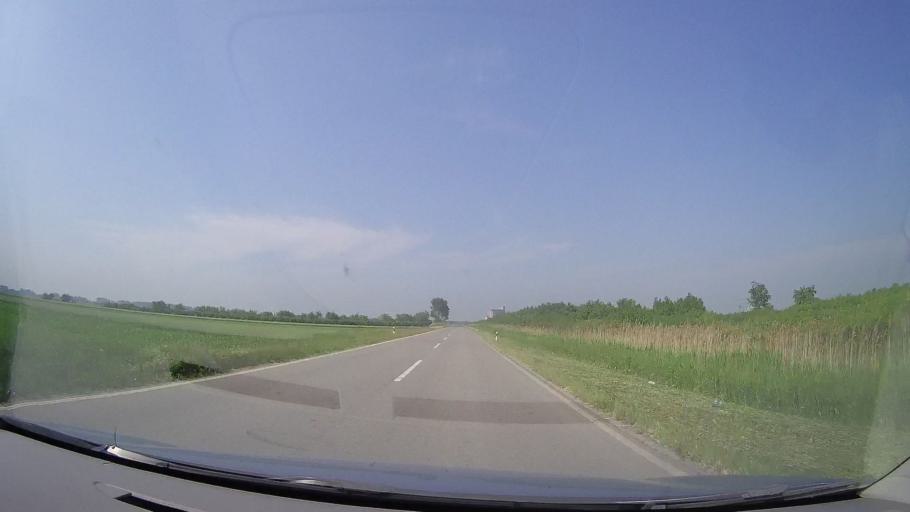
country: RS
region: Autonomna Pokrajina Vojvodina
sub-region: Srednjebanatski Okrug
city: Secanj
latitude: 45.3813
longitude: 20.7889
